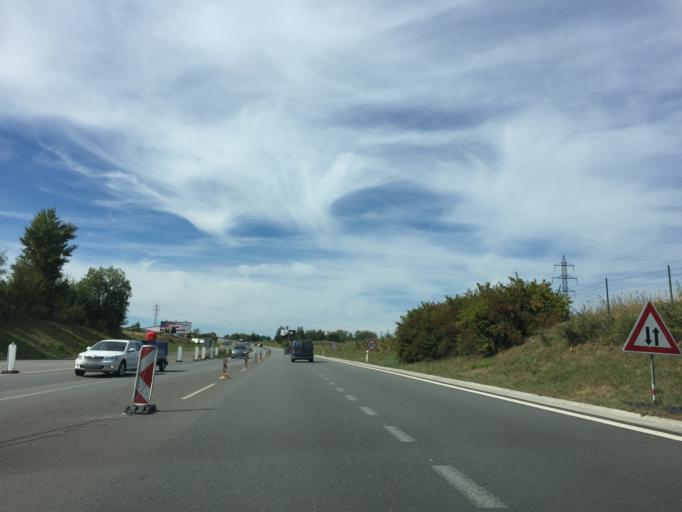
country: CZ
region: Jihocesky
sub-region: Okres Tabor
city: Sezimovo Usti
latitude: 49.4067
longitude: 14.7172
